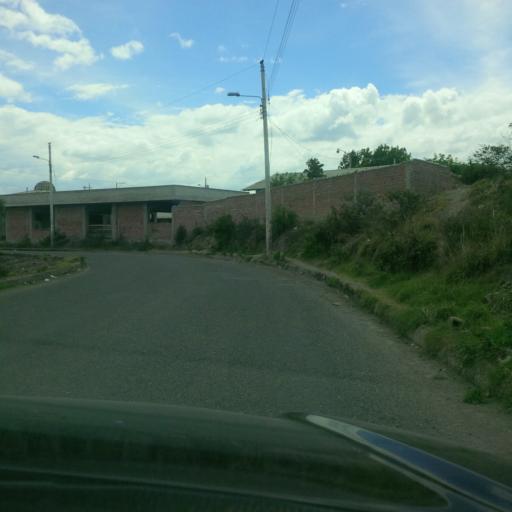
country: EC
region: Chimborazo
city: Riobamba
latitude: -1.6523
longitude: -78.6493
